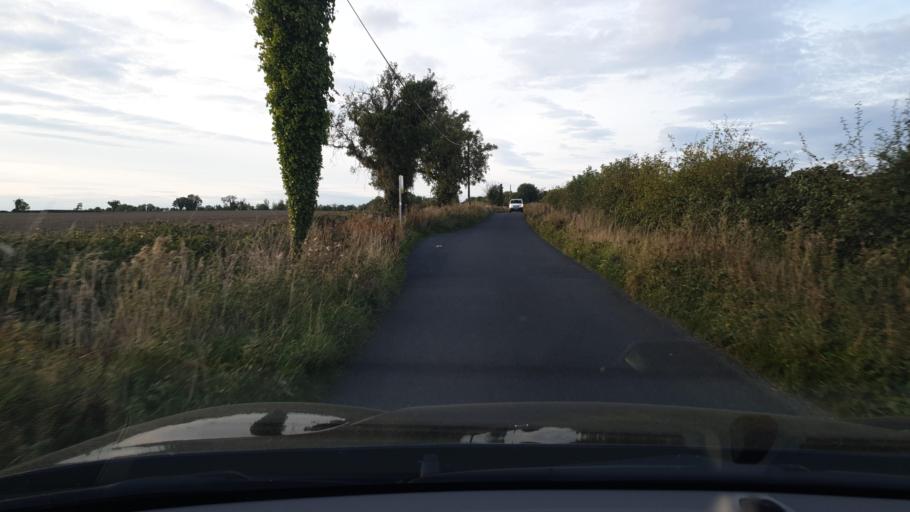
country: IE
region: Leinster
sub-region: An Mhi
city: Ashbourne
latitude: 53.5201
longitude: -6.3859
